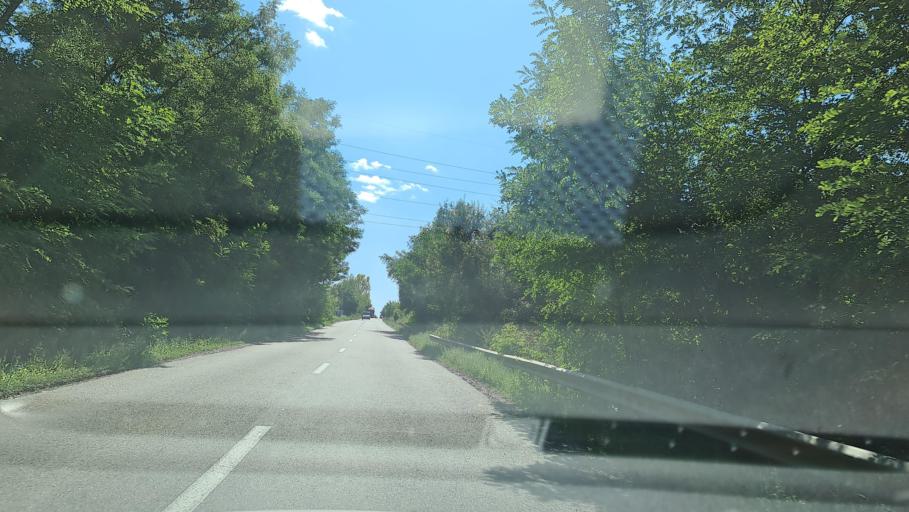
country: RO
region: Bacau
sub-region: Comuna Scorteni
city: Scorteni
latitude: 46.5571
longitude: 26.6228
